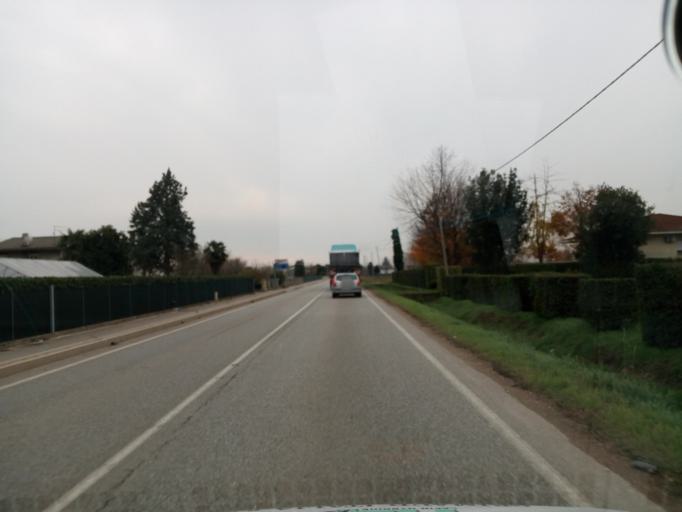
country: IT
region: Veneto
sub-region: Provincia di Treviso
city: Fanzolo
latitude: 45.7162
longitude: 12.0149
